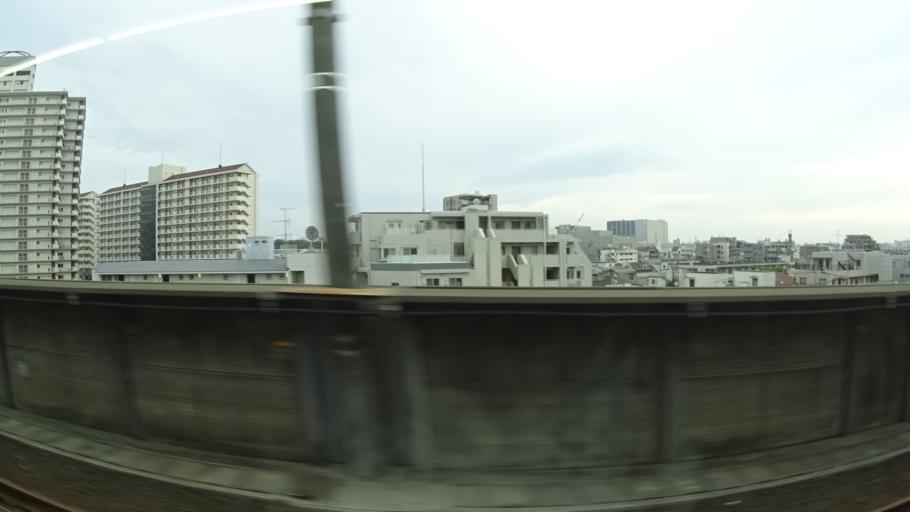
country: JP
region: Saitama
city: Kawaguchi
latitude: 35.7887
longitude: 139.7031
